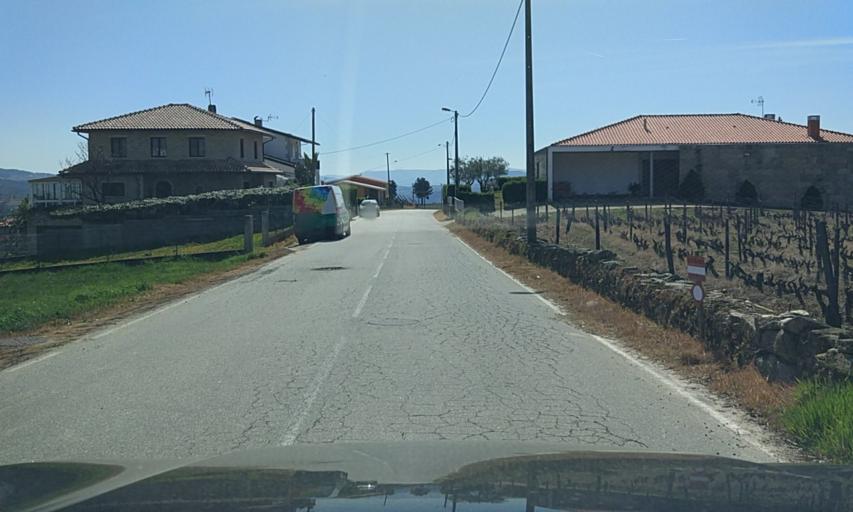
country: PT
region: Vila Real
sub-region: Sabrosa
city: Sabrosa
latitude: 41.3244
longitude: -7.5551
